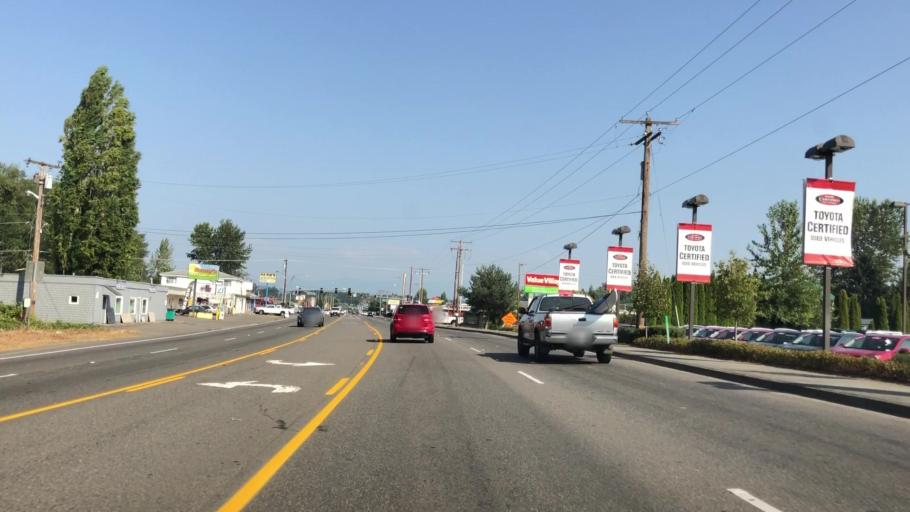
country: US
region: Washington
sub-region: Pierce County
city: Puyallup
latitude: 47.2030
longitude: -122.3108
